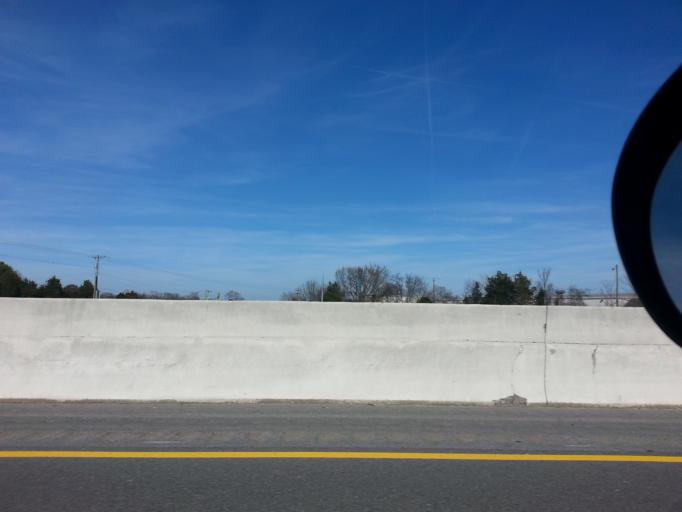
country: US
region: Tennessee
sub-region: Davidson County
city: Oak Hill
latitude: 36.0682
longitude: -86.6884
